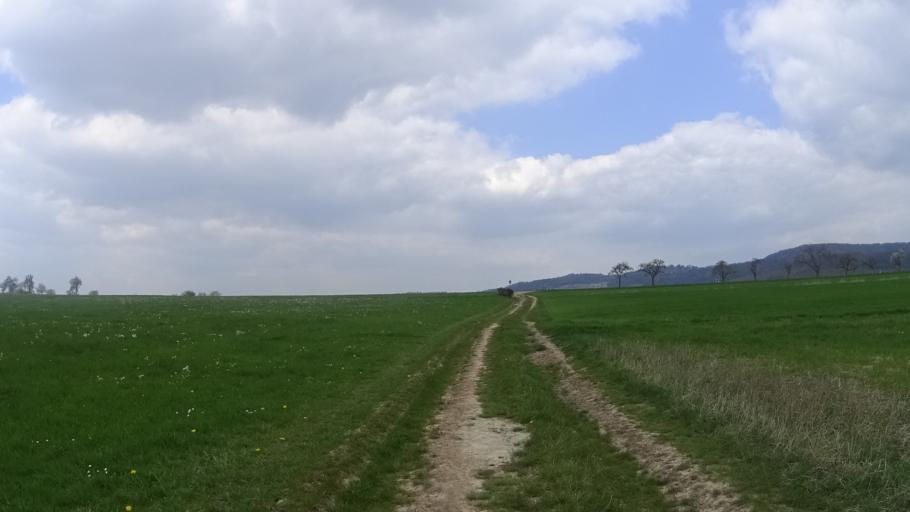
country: DE
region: Bavaria
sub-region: Upper Franconia
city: Kleinsendelbach
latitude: 49.6055
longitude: 11.1779
